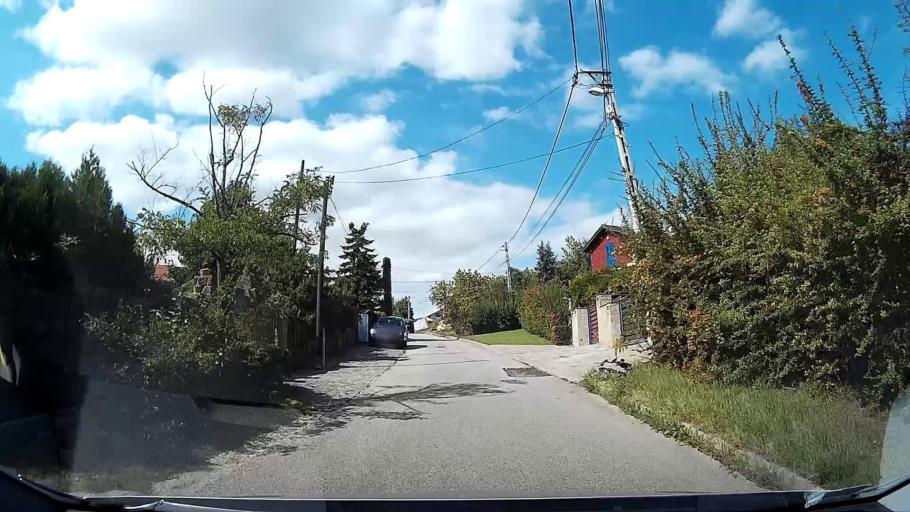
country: HU
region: Pest
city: Szentendre
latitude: 47.6893
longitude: 19.0725
